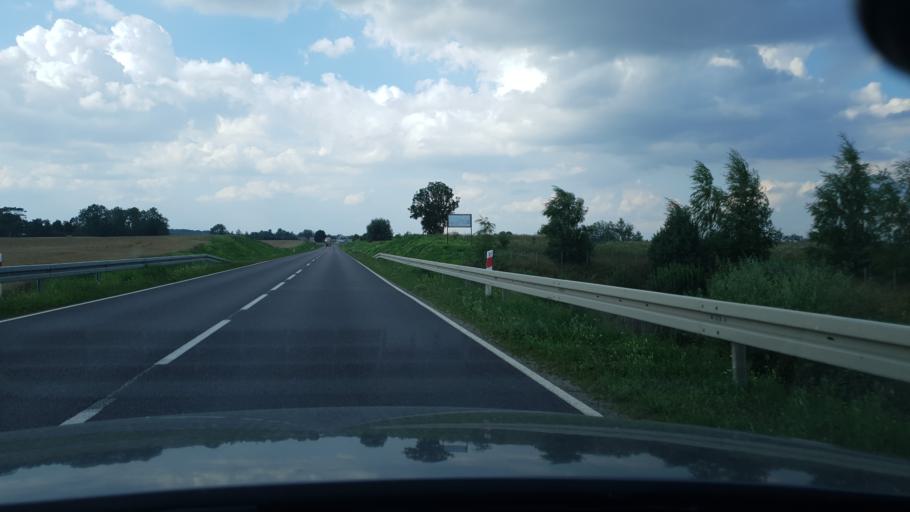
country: PL
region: Kujawsko-Pomorskie
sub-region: Powiat wabrzeski
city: Wabrzezno
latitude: 53.2885
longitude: 18.9273
